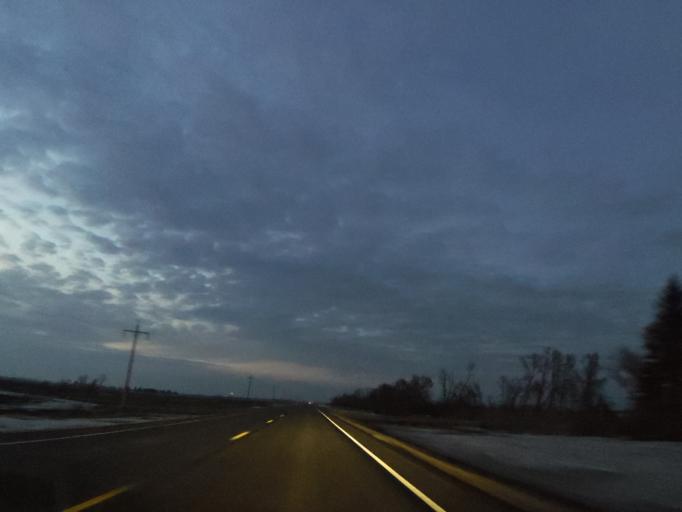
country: US
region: North Dakota
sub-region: Walsh County
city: Park River
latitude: 48.2373
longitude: -97.6226
